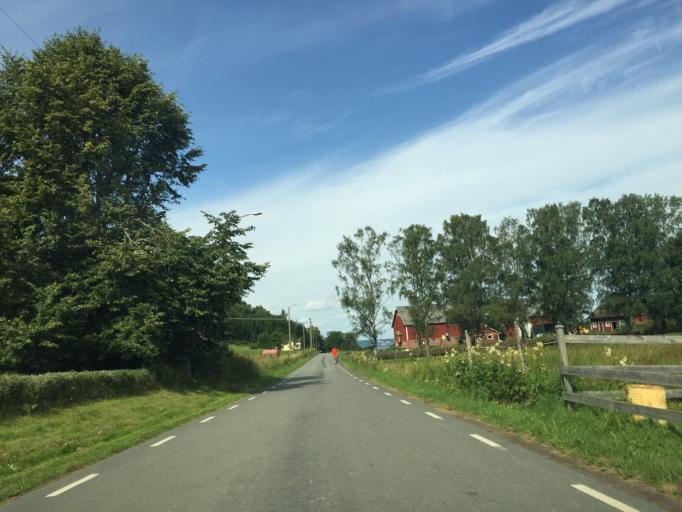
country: SE
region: Joenkoeping
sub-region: Jonkopings Kommun
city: Kaxholmen
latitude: 57.8562
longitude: 14.2812
